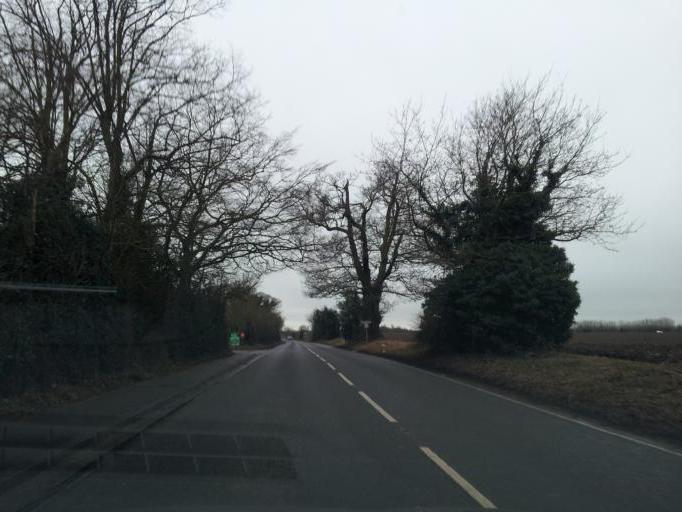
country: GB
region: England
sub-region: Essex
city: Manningtree
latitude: 51.9385
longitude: 1.0627
